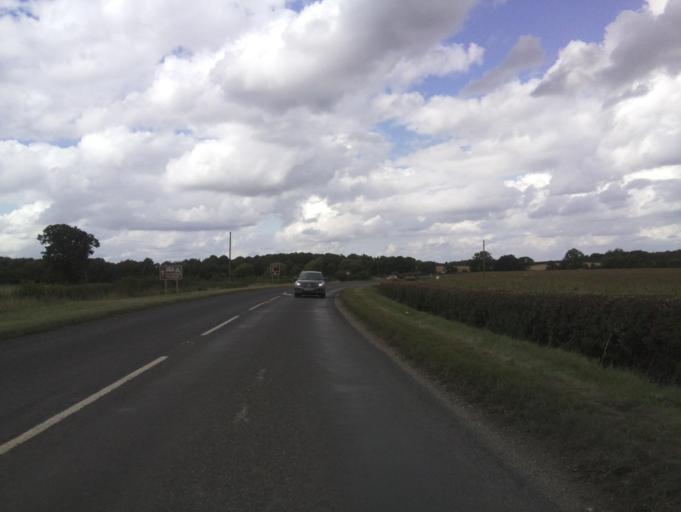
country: GB
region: England
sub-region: North Yorkshire
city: Ripon
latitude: 54.1734
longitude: -1.5531
